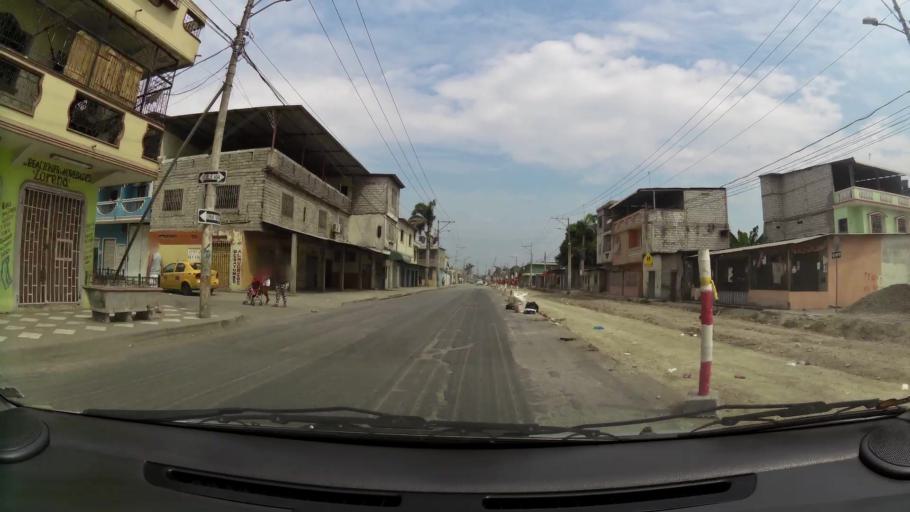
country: EC
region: Guayas
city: Guayaquil
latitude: -2.2416
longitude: -79.9251
